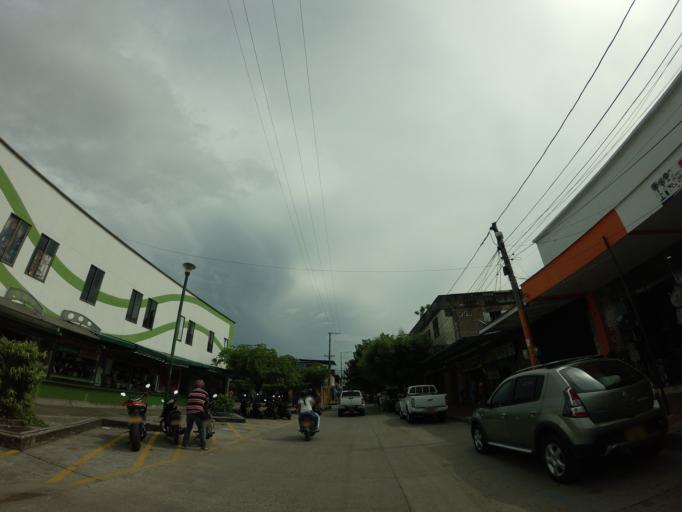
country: CO
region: Caldas
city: La Dorada
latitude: 5.4540
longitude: -74.6645
